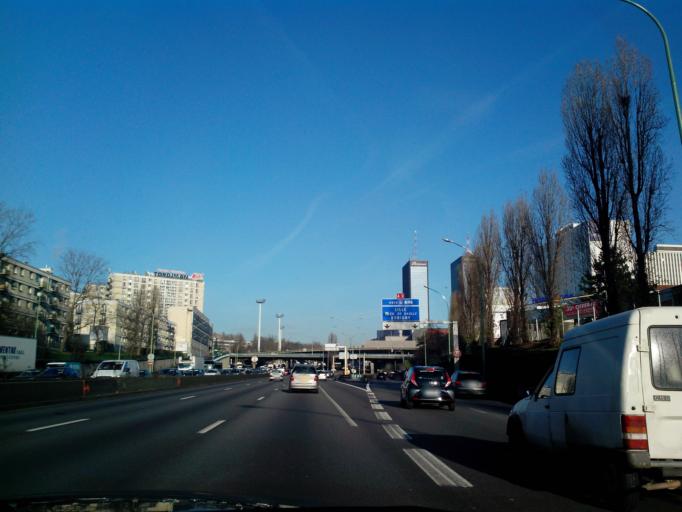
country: FR
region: Ile-de-France
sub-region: Departement de Seine-Saint-Denis
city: Bagnolet
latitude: 48.8612
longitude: 2.4140
